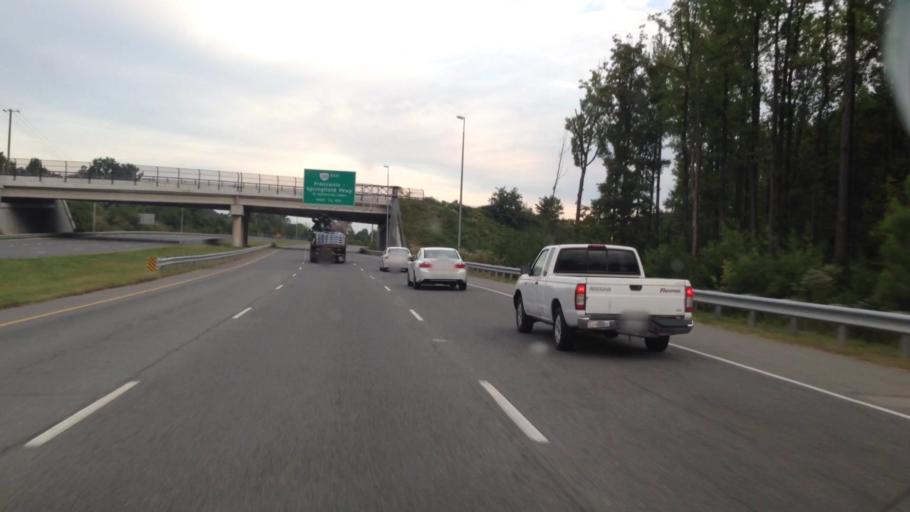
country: US
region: Virginia
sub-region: Fairfax County
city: West Springfield
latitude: 38.7515
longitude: -77.2133
